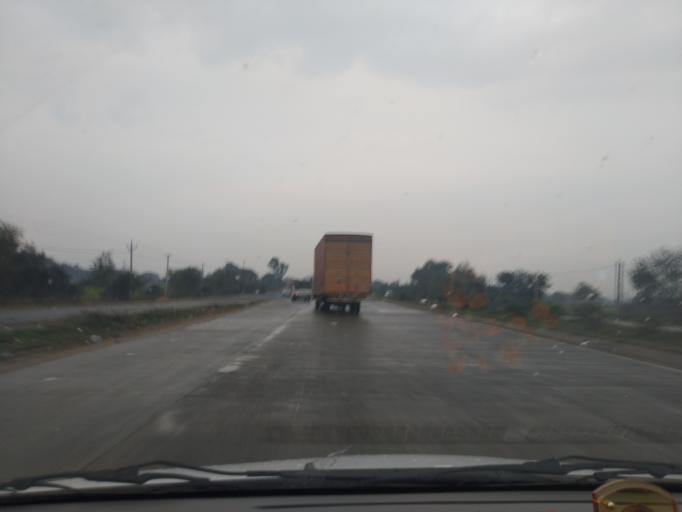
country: IN
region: Bihar
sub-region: Kaimur District
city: Bhabua
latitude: 25.1061
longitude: 83.7043
